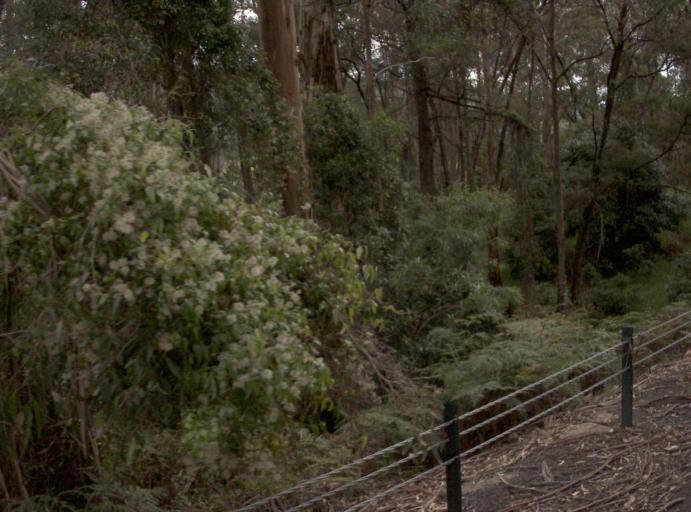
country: AU
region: New South Wales
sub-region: Bombala
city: Bombala
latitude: -37.4705
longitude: 149.1772
